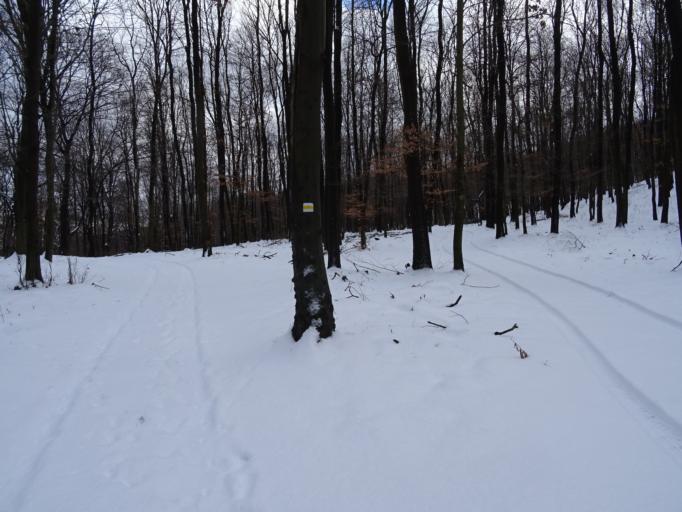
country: HU
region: Komarom-Esztergom
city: Oroszlany
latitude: 47.4674
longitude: 18.3902
